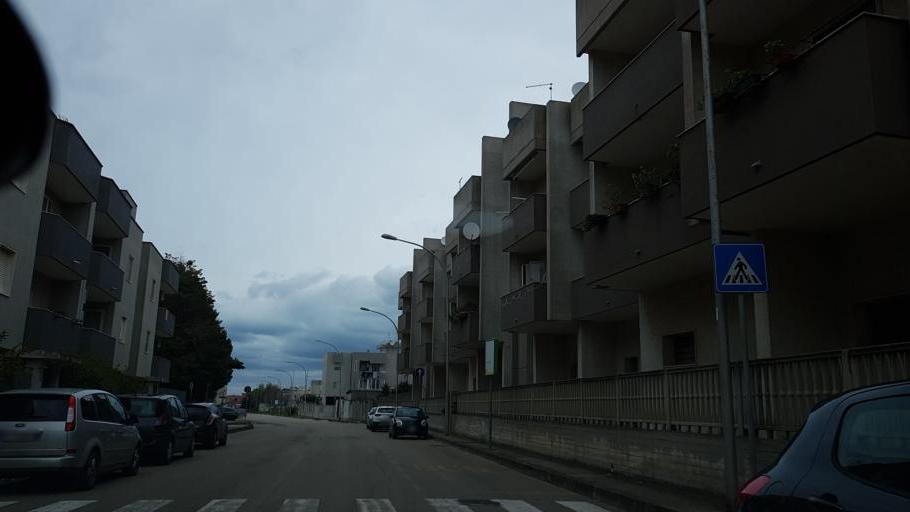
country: IT
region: Apulia
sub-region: Provincia di Brindisi
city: La Rosa
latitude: 40.6035
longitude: 17.9517
